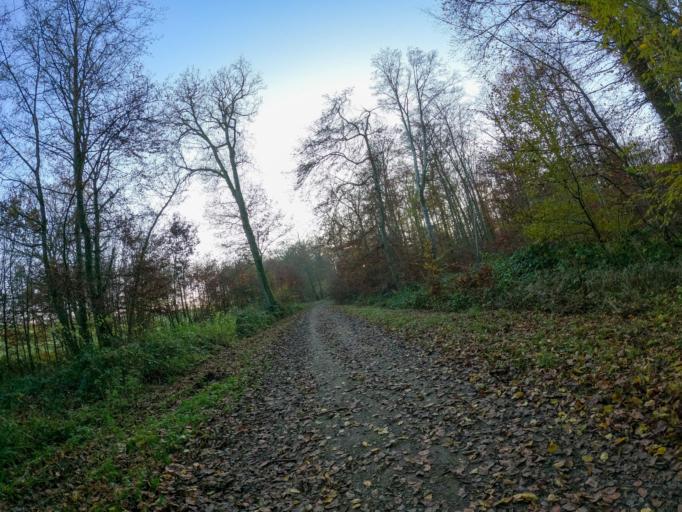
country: LU
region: Luxembourg
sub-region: Canton de Capellen
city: Dippach
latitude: 49.5997
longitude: 6.0009
